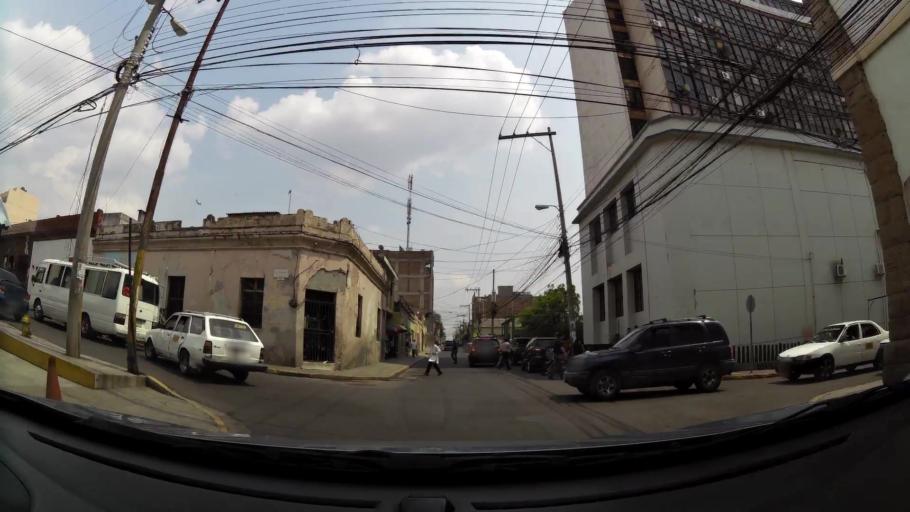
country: HN
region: Francisco Morazan
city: Tegucigalpa
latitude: 14.1092
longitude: -87.2090
